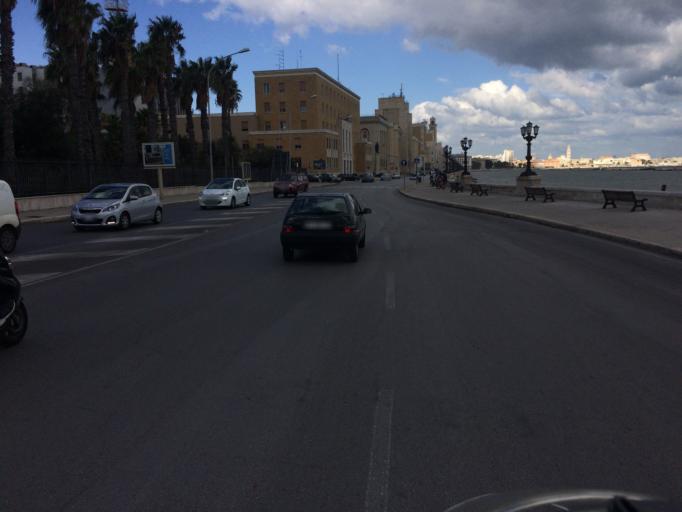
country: IT
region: Apulia
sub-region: Provincia di Bari
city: Bari
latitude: 41.1193
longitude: 16.8894
